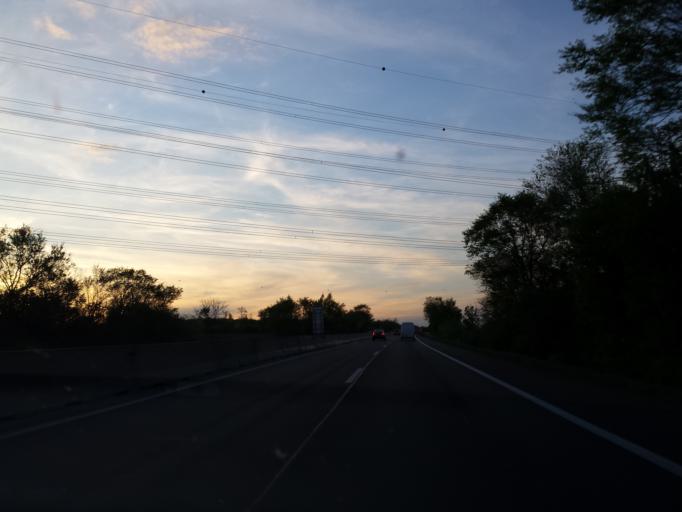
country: AT
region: Lower Austria
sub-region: Politischer Bezirk Ganserndorf
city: Orth an der Donau
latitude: 48.0741
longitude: 16.6829
